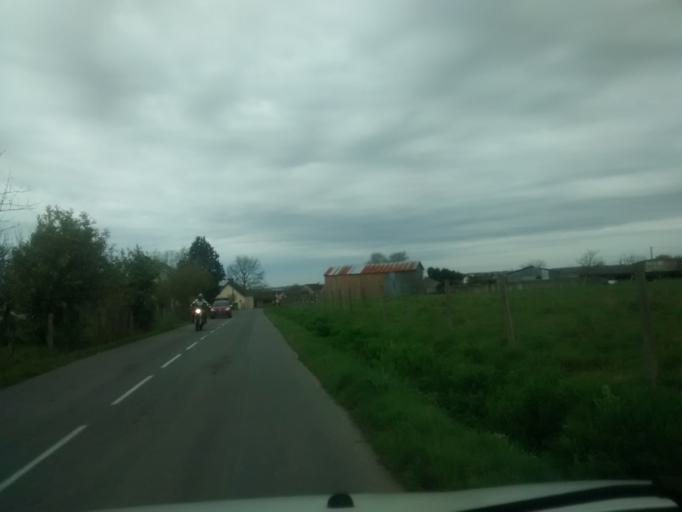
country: FR
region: Brittany
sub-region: Departement d'Ille-et-Vilaine
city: Betton
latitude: 48.1793
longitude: -1.6188
